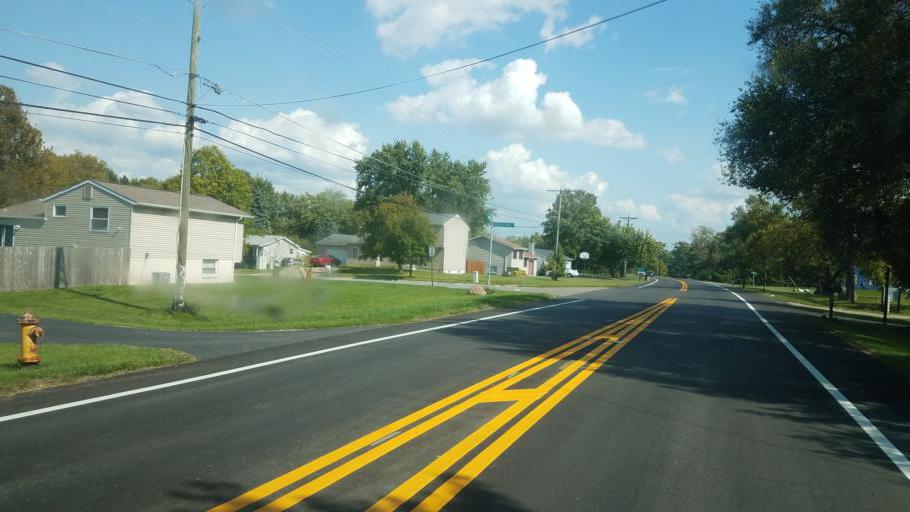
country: US
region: Ohio
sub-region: Franklin County
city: Grove City
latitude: 39.9159
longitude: -83.0909
